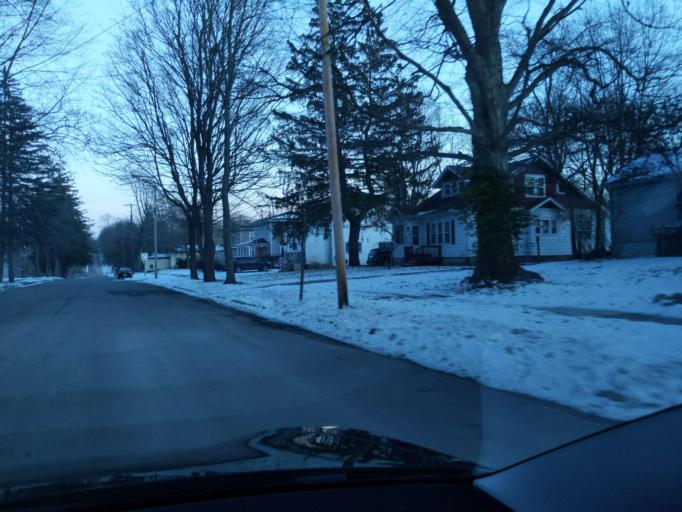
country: US
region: Michigan
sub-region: Ingham County
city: Mason
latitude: 42.5772
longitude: -84.4477
